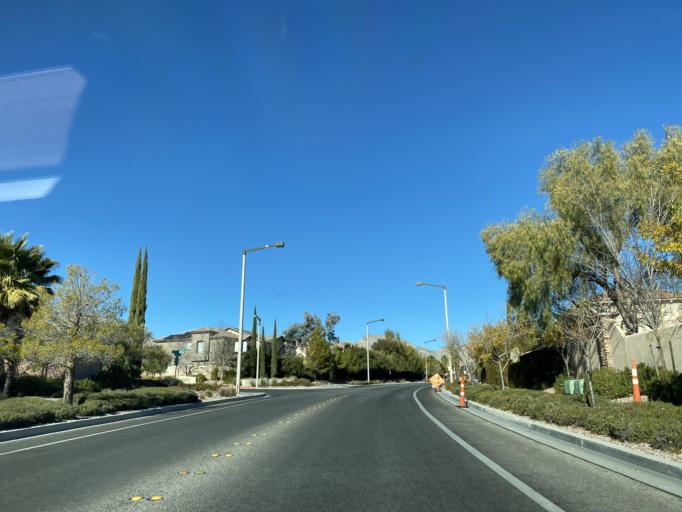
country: US
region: Nevada
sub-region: Clark County
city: Summerlin South
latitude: 36.1629
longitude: -115.3489
